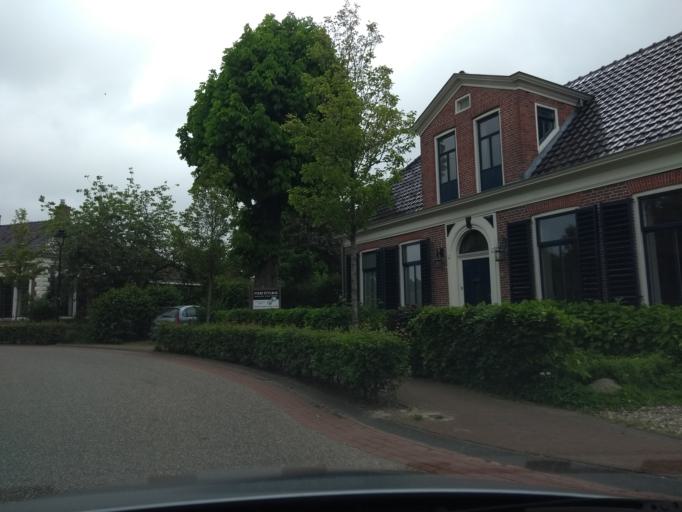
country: NL
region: Groningen
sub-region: Gemeente Zuidhorn
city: Oldehove
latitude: 53.3400
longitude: 6.4253
